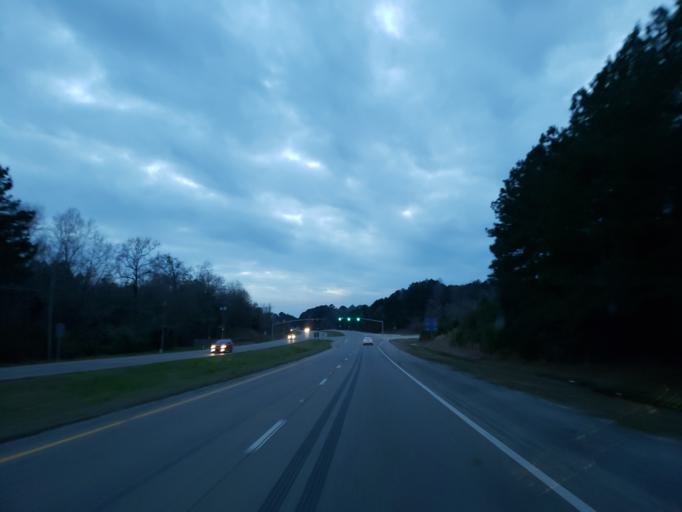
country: US
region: Mississippi
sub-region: Lauderdale County
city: Marion
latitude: 32.3667
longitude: -88.6512
